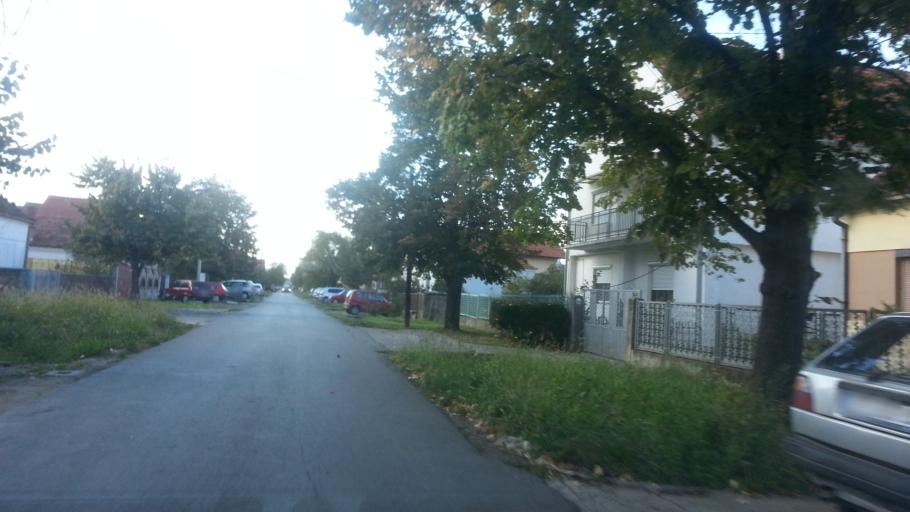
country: RS
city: Novi Banovci
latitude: 44.9075
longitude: 20.2665
